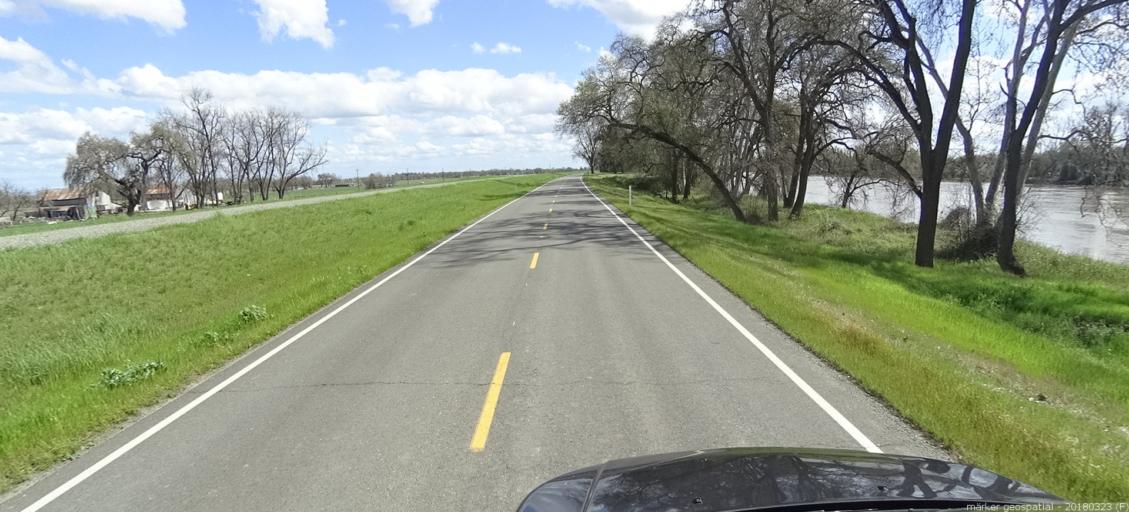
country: US
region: California
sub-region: Yolo County
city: West Sacramento
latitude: 38.6648
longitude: -121.6120
